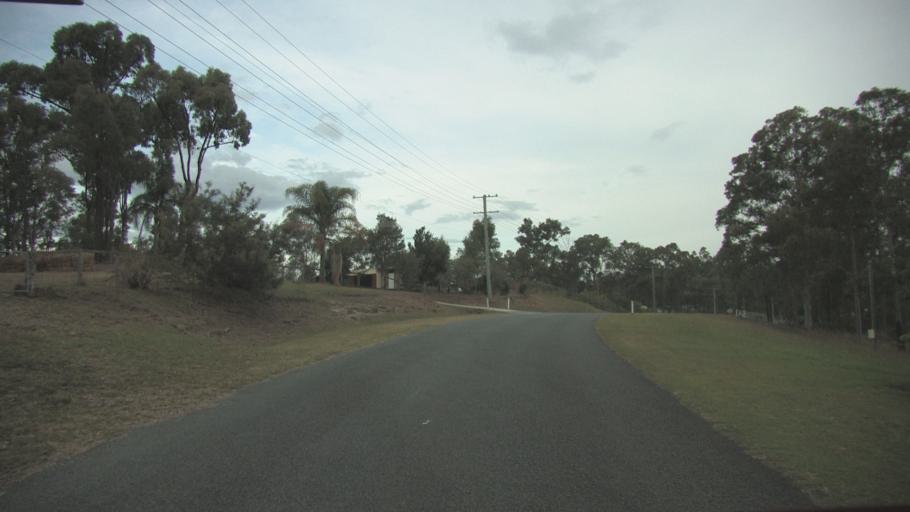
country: AU
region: Queensland
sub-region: Logan
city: Chambers Flat
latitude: -27.8224
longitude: 153.0951
